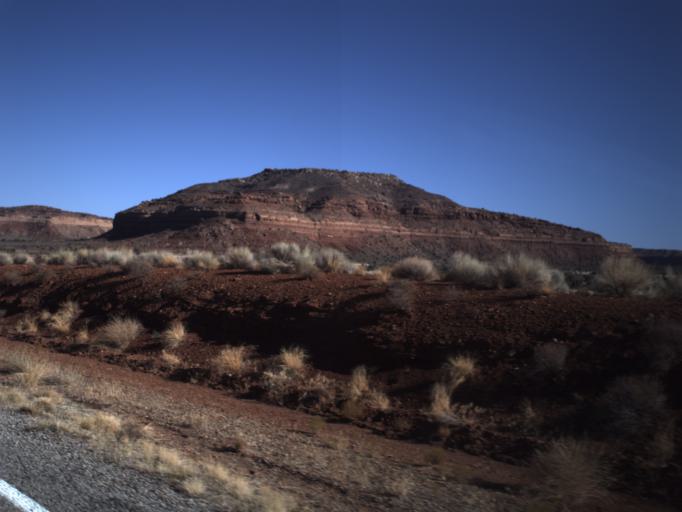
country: US
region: Utah
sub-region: San Juan County
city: Blanding
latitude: 37.7207
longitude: -110.2468
